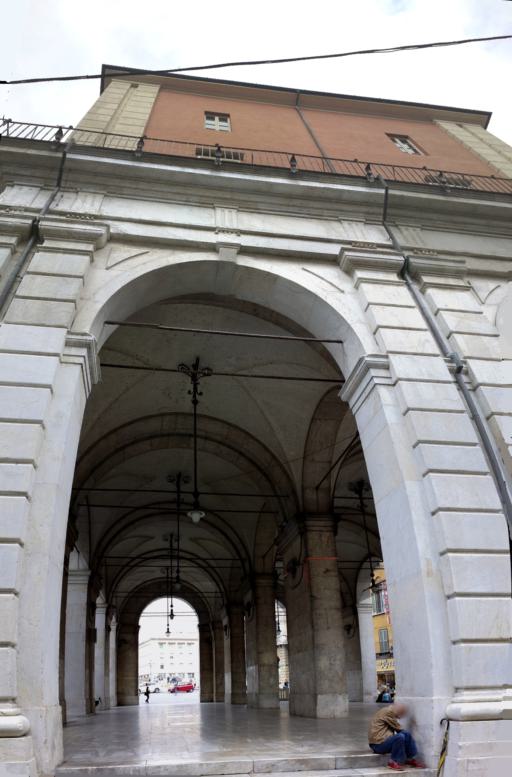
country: IT
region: Tuscany
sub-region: Province of Pisa
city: Pisa
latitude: 43.7151
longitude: 10.4012
